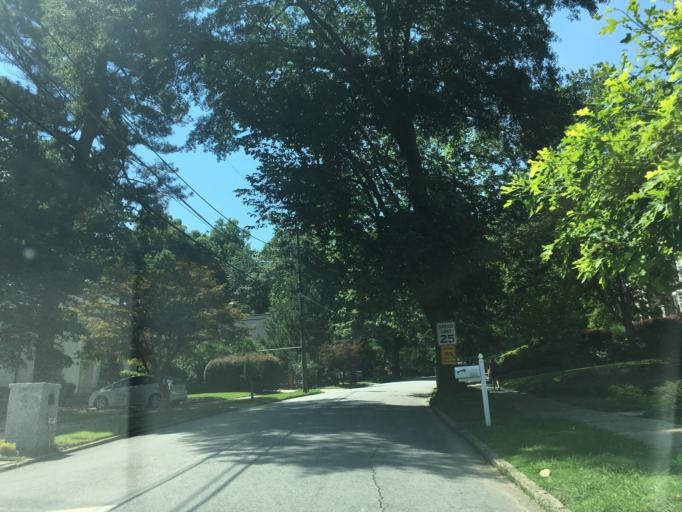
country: US
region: Georgia
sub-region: DeKalb County
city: Druid Hills
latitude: 33.8000
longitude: -84.3607
